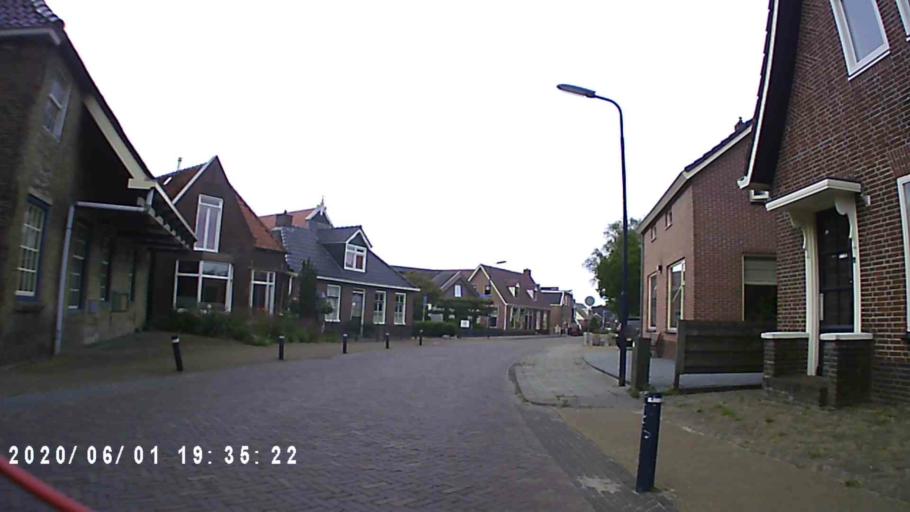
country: NL
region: Friesland
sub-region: Gemeente Achtkarspelen
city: Augustinusga
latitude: 53.2185
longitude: 6.1629
